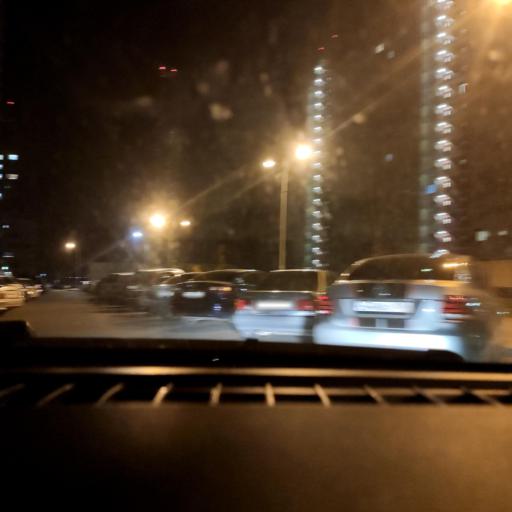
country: RU
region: Voronezj
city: Somovo
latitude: 51.6702
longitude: 39.3214
